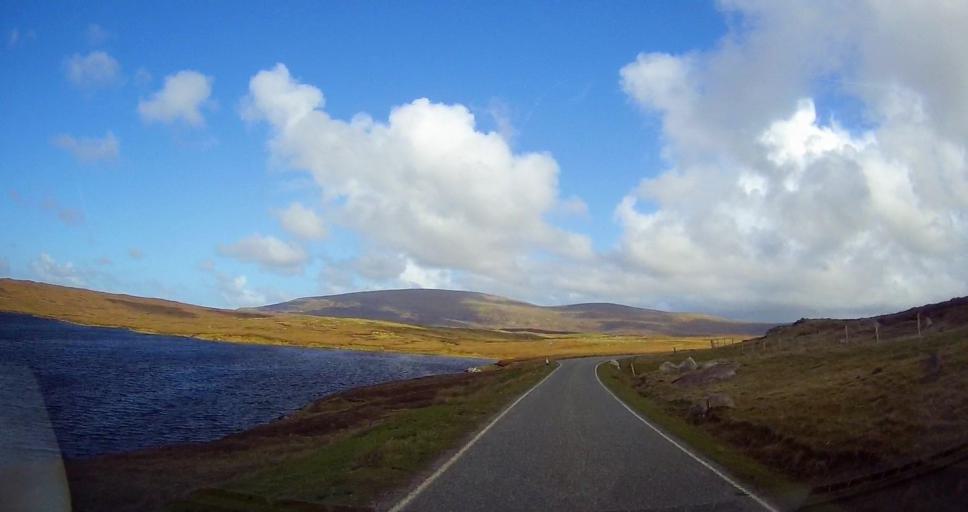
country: GB
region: Scotland
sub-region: Shetland Islands
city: Lerwick
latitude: 60.4922
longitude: -1.3910
